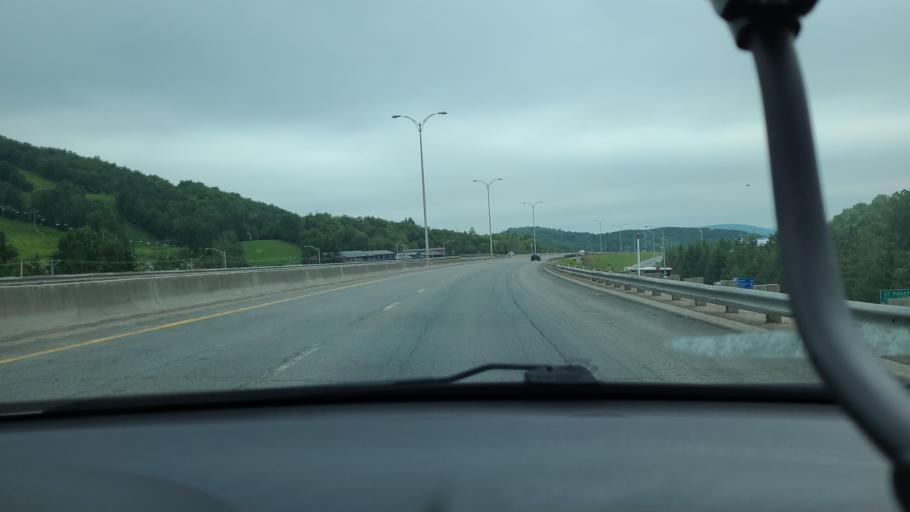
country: CA
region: Quebec
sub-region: Laurentides
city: Mont-Tremblant
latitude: 46.1109
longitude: -74.4794
